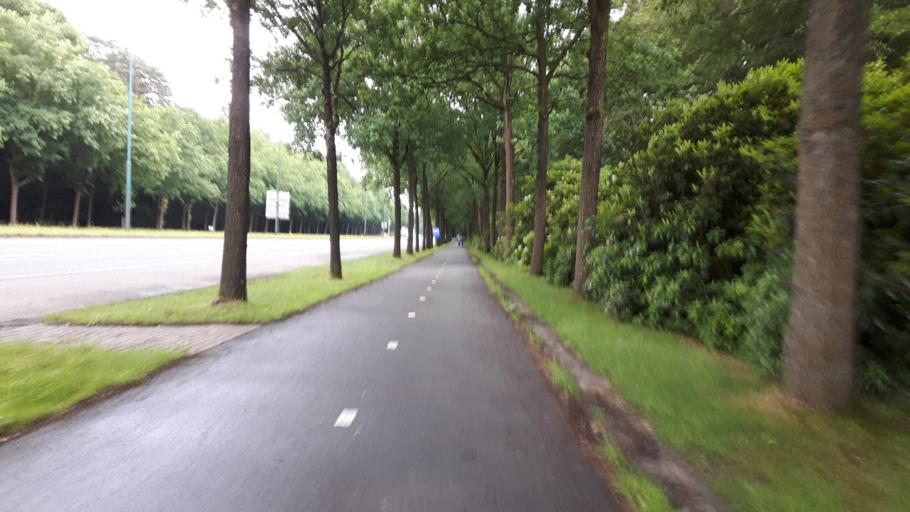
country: NL
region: Utrecht
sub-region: Gemeente Baarn
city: Baarn
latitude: 52.1997
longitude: 5.2769
